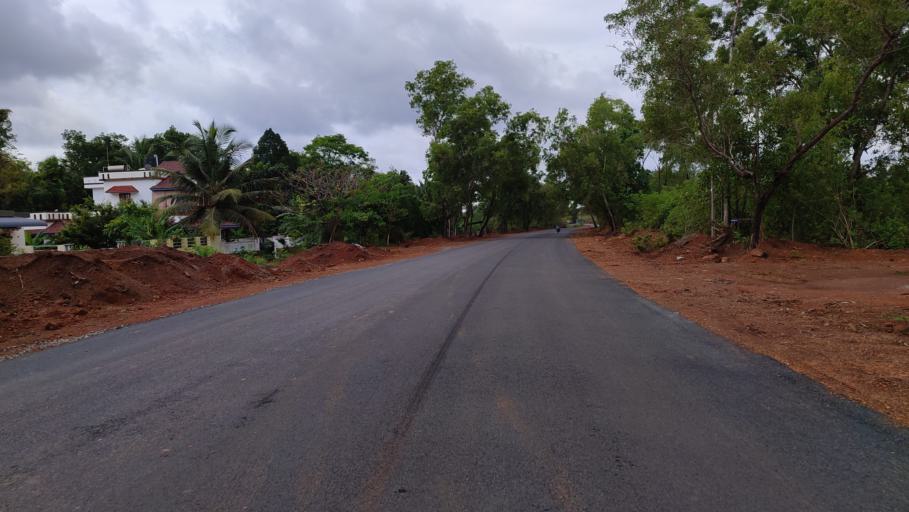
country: IN
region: Kerala
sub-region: Kasaragod District
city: Kasaragod
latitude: 12.5527
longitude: 75.0712
